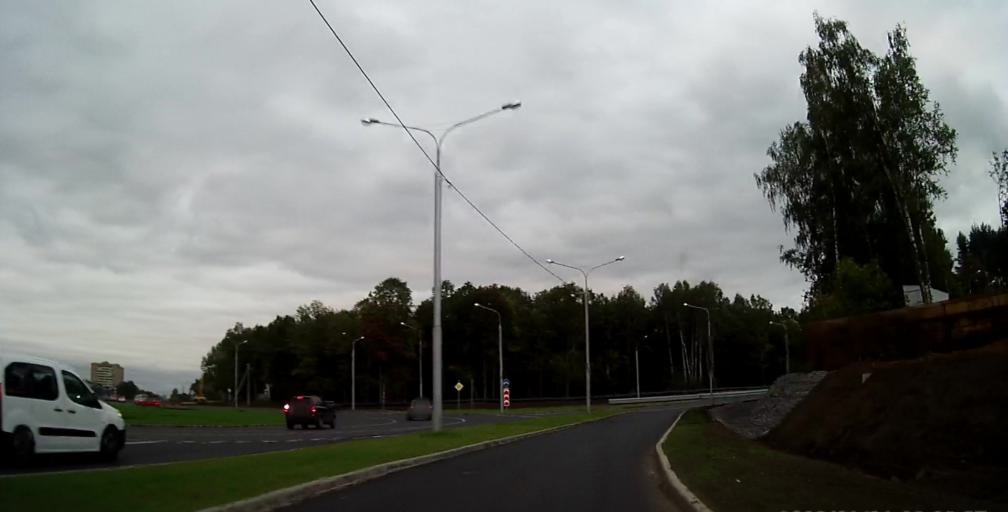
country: RU
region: Moskovskaya
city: Dubrovitsy
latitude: 55.4146
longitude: 37.4920
